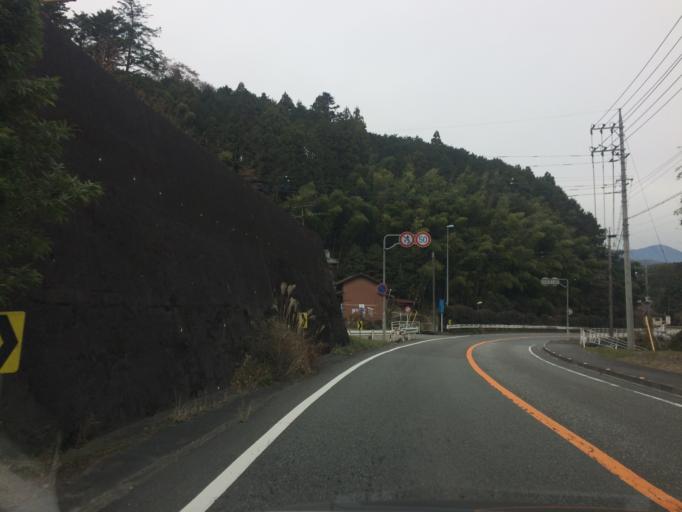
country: JP
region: Shizuoka
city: Fujinomiya
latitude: 35.2730
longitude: 138.4516
